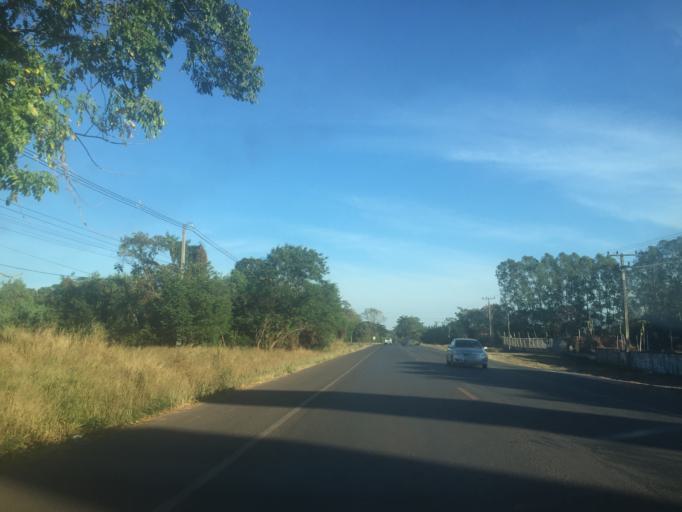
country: TH
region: Changwat Udon Thani
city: Si That
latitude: 16.9714
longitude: 103.2339
